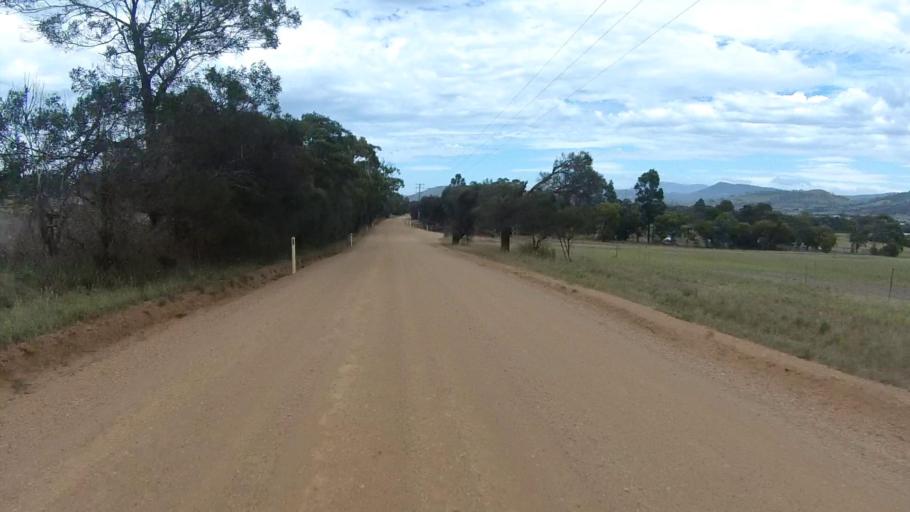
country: AU
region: Tasmania
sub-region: Clarence
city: Cambridge
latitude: -42.7049
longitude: 147.4570
